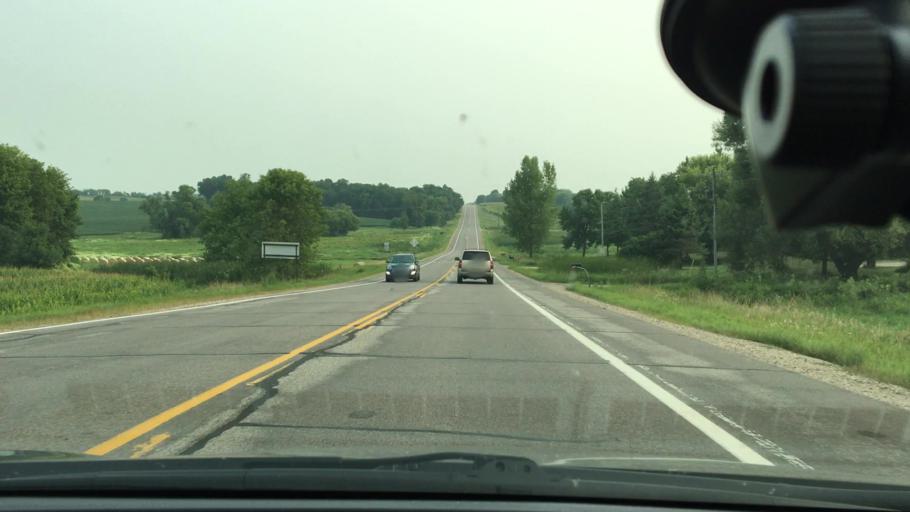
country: US
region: Minnesota
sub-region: Wright County
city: Albertville
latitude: 45.2881
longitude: -93.6637
